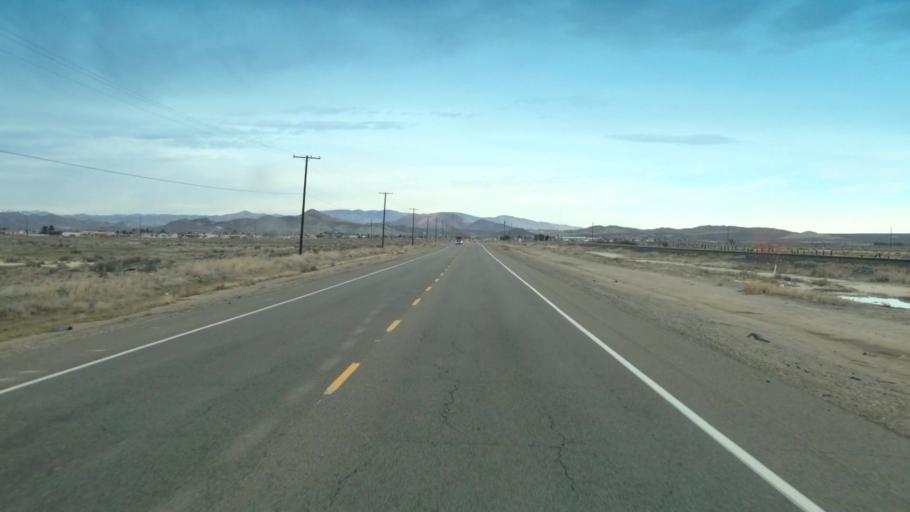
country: US
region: California
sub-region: Kern County
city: Rosamond
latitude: 34.8153
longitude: -118.1552
